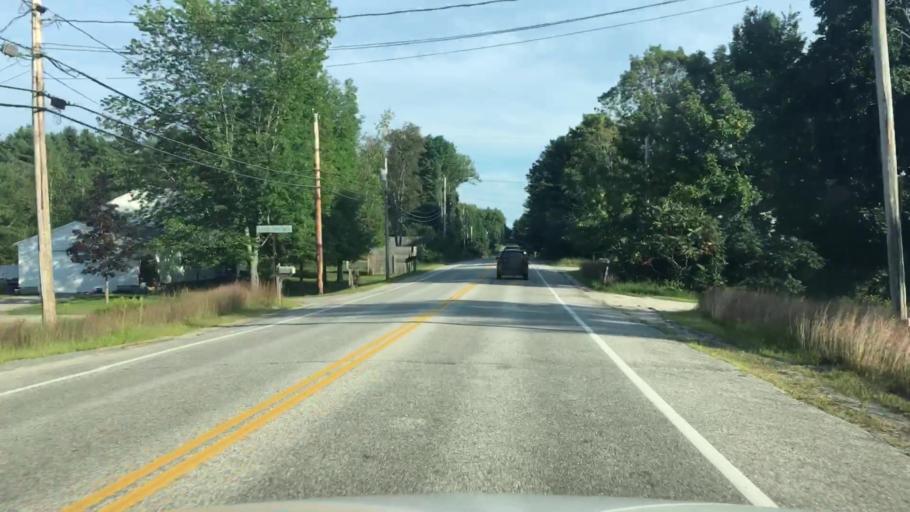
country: US
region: Maine
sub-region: Cumberland County
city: South Windham
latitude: 43.7438
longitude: -70.4238
